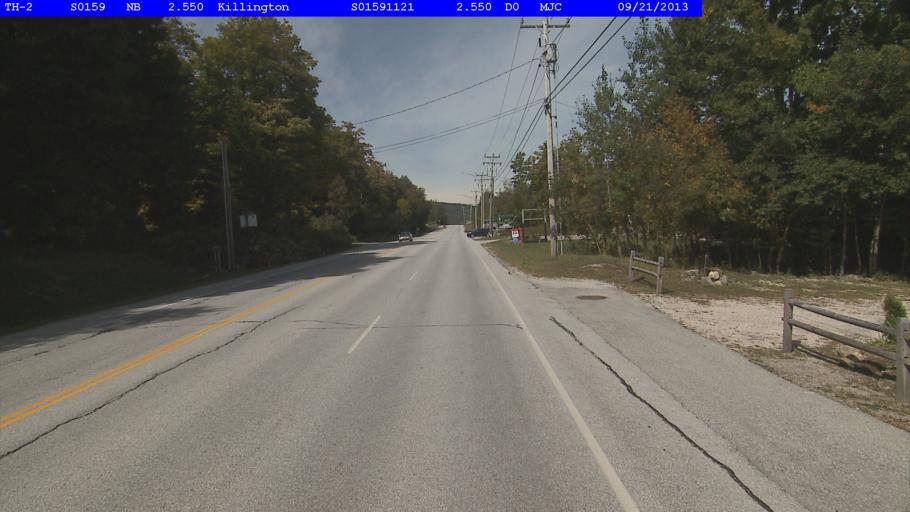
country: US
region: Vermont
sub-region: Rutland County
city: Rutland
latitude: 43.6629
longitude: -72.7991
